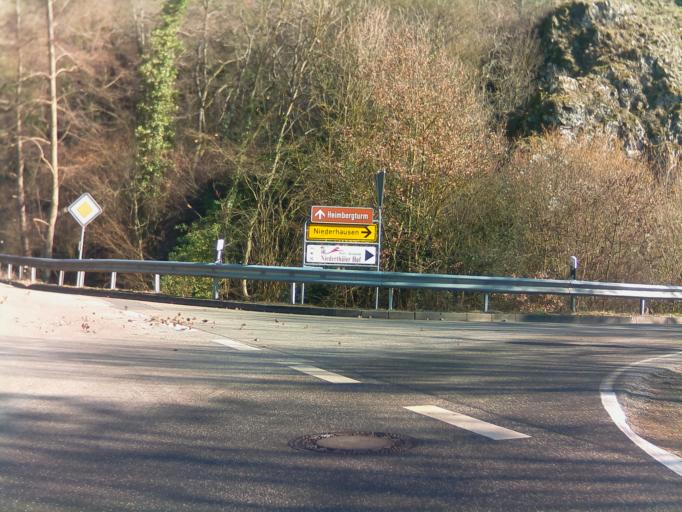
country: DE
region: Rheinland-Pfalz
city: Schlossbockelheim
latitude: 49.8047
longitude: 7.7387
